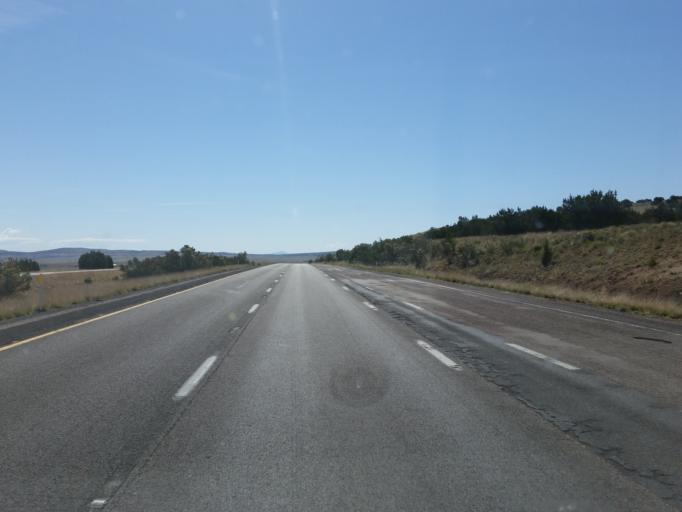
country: US
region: Arizona
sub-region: Mohave County
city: Peach Springs
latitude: 35.3192
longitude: -112.8889
